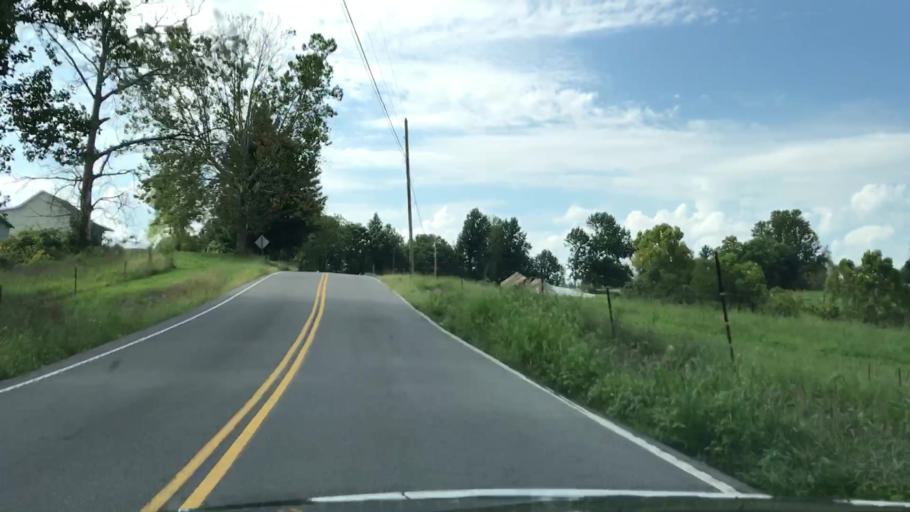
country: US
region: Tennessee
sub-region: Sumner County
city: Westmoreland
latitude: 36.5074
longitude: -86.1863
